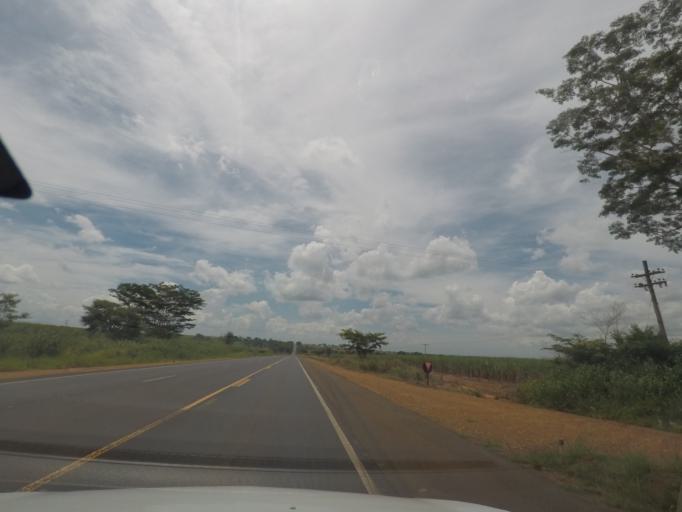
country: BR
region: Sao Paulo
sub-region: Barretos
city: Barretos
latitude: -20.4125
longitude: -48.6331
